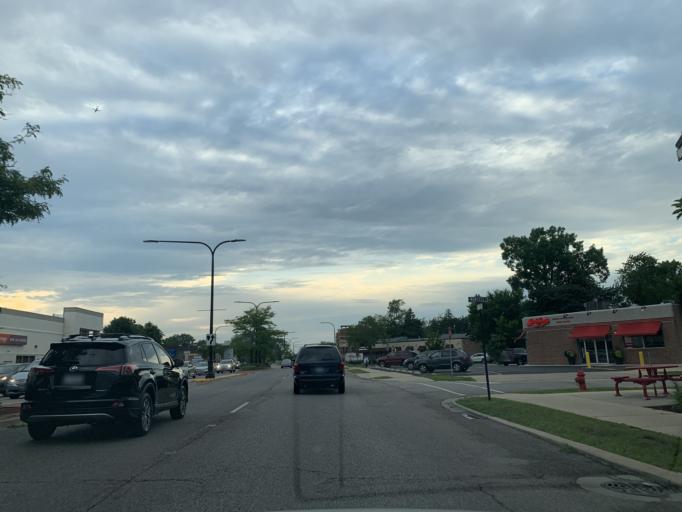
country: US
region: Illinois
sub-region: Cook County
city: Lincolnwood
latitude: 41.9985
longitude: -87.7204
